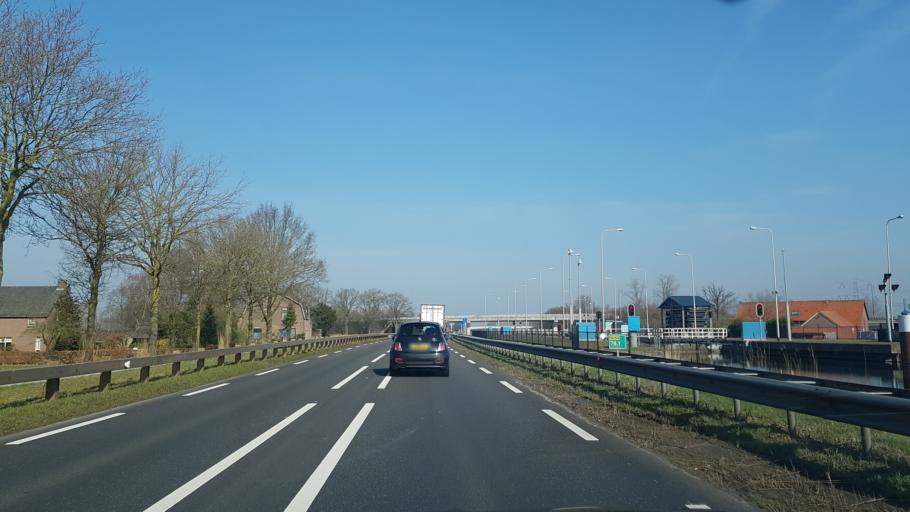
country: NL
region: North Brabant
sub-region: Gemeente Someren
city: Someren
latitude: 51.4150
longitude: 5.7015
